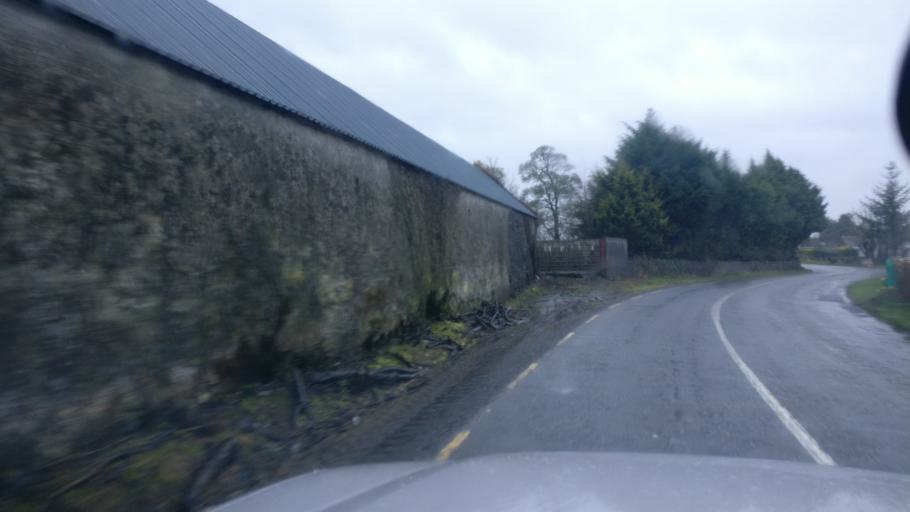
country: IE
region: Connaught
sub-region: County Galway
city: Ballinasloe
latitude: 53.2533
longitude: -8.1777
